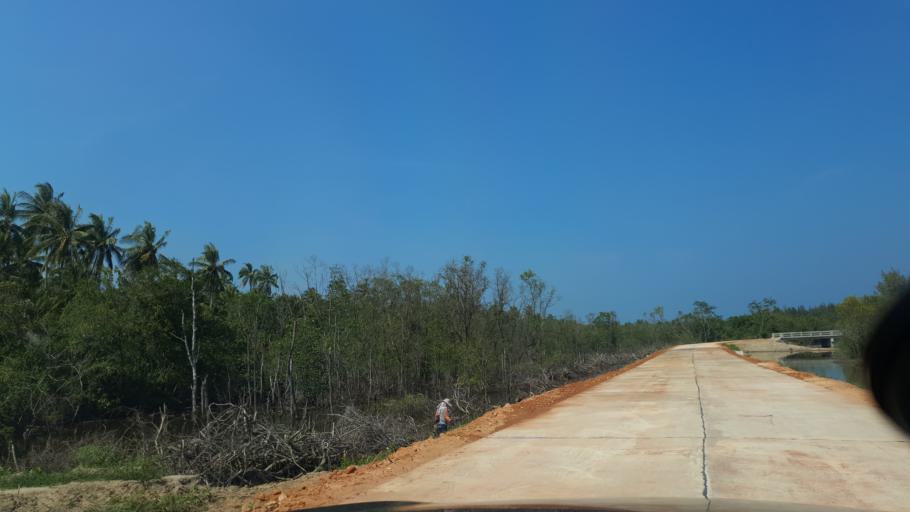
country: TH
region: Surat Thani
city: Tha Chana
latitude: 9.5928
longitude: 99.2077
